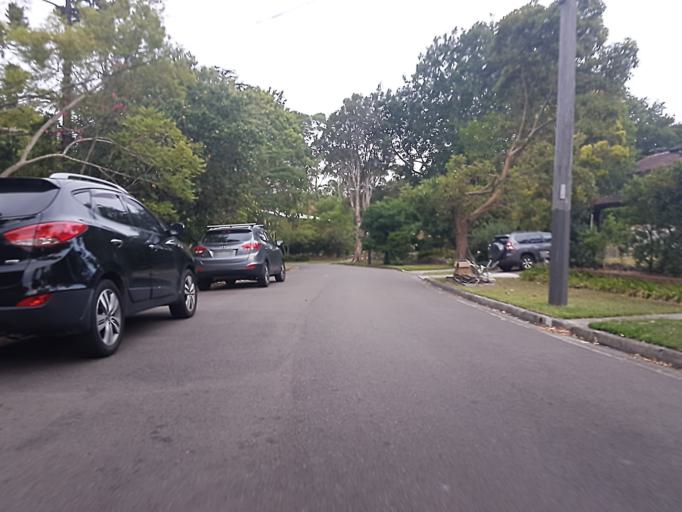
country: AU
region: New South Wales
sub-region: Warringah
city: Forestville
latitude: -33.7540
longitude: 151.2198
